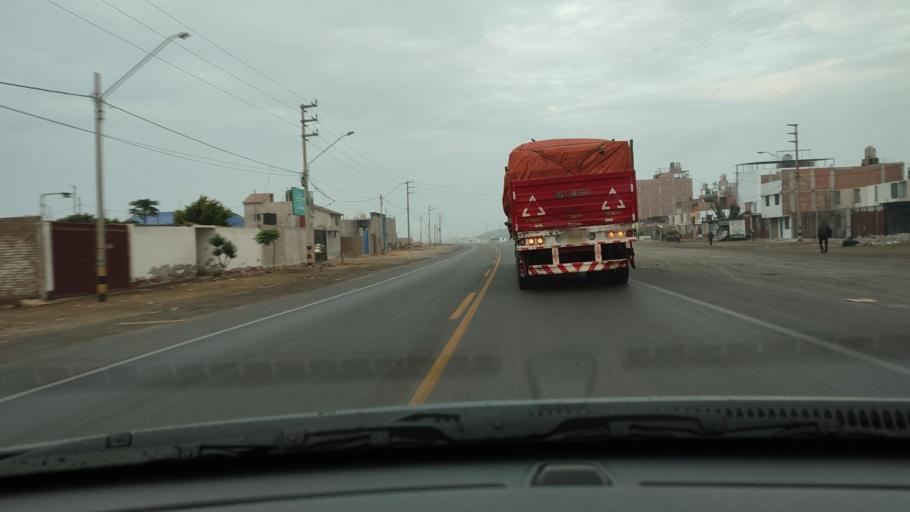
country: PE
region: La Libertad
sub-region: Provincia de Trujillo
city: Huanchaco
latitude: -8.0954
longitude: -79.0986
